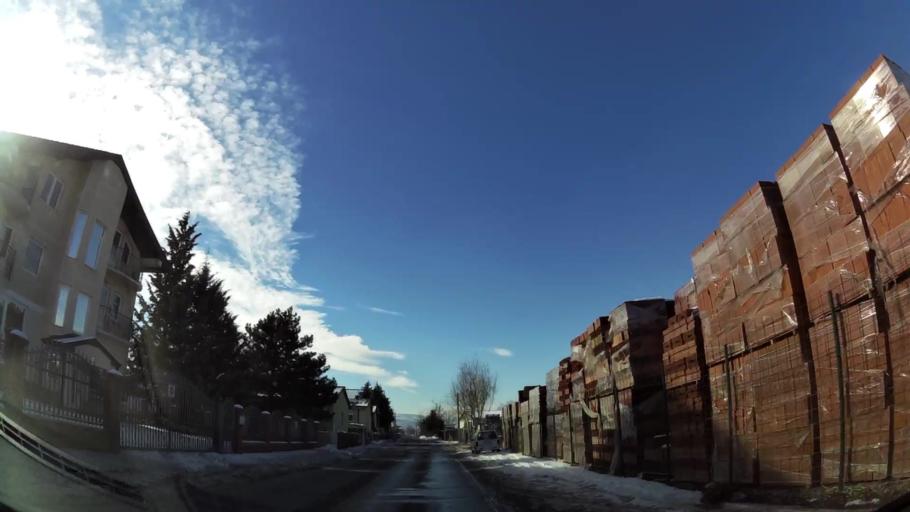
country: MK
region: Saraj
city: Saraj
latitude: 42.0109
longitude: 21.3447
